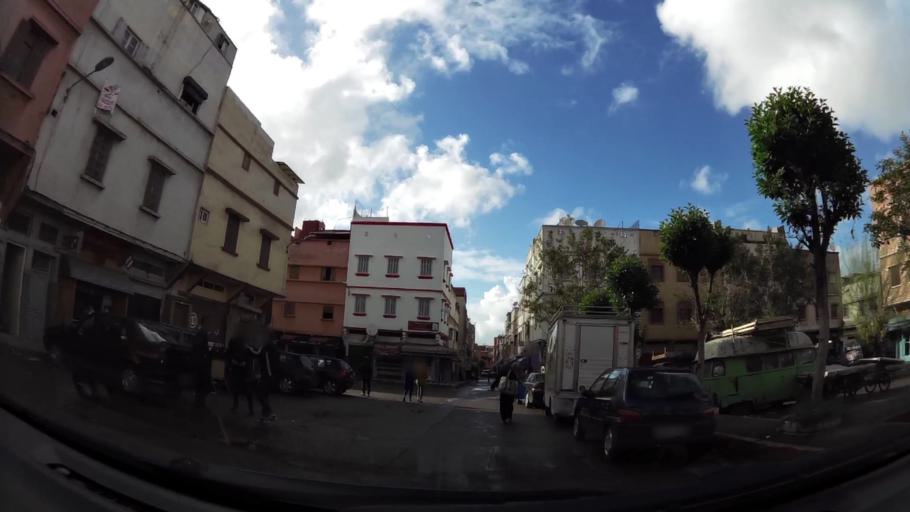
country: MA
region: Grand Casablanca
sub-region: Casablanca
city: Casablanca
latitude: 33.5511
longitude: -7.5911
